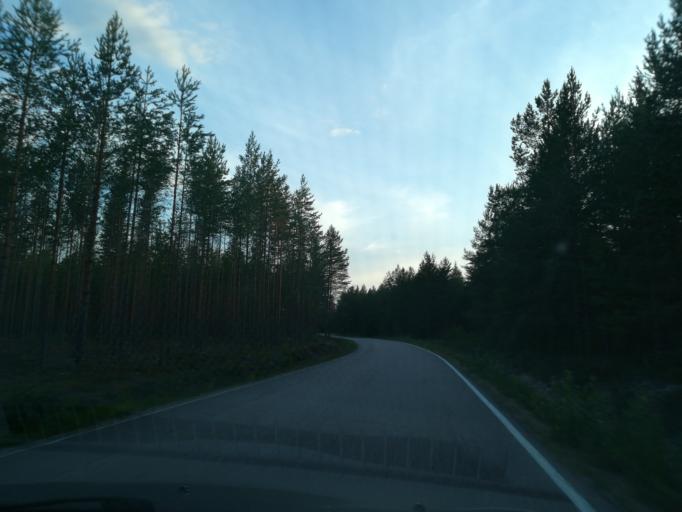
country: FI
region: South Karelia
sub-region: Lappeenranta
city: Joutseno
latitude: 61.3461
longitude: 28.4207
